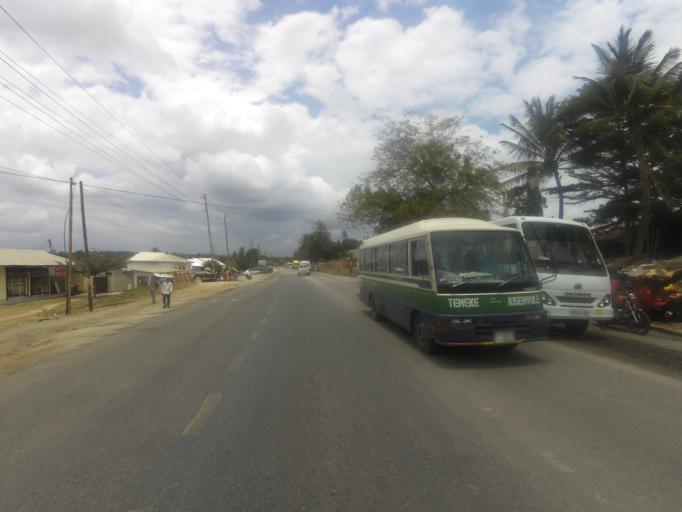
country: TZ
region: Pwani
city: Vikindu
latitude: -6.9489
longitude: 39.2811
